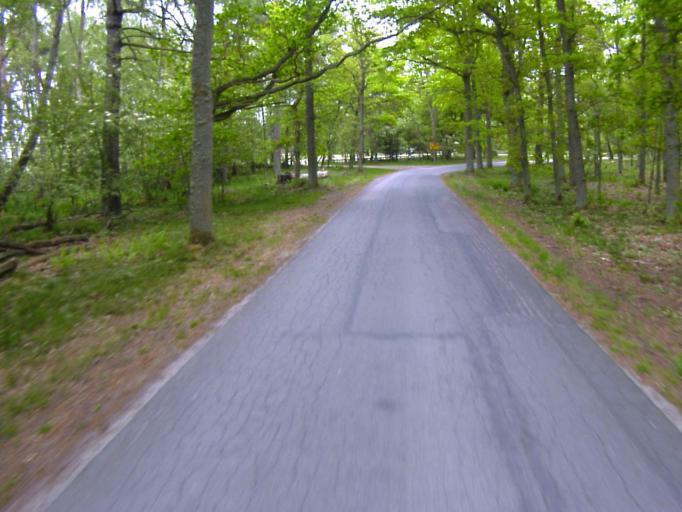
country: SE
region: Skane
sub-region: Kristianstads Kommun
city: Ahus
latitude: 55.9199
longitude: 14.3195
